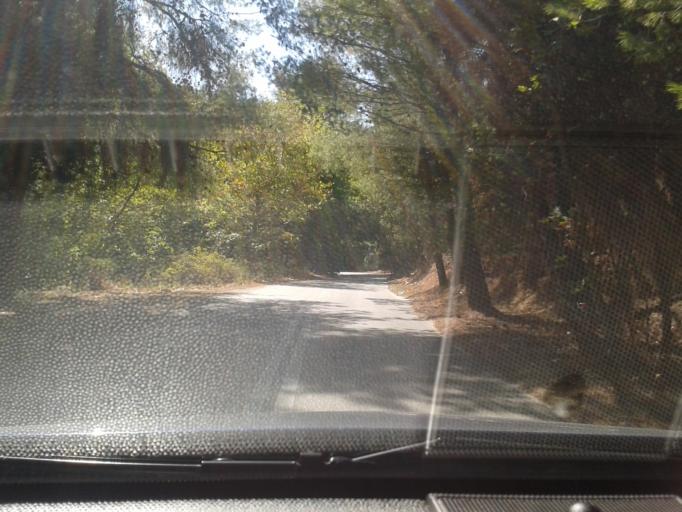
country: GR
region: Attica
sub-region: Nomarchia Anatolikis Attikis
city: Varybobi
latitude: 38.1315
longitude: 23.7870
